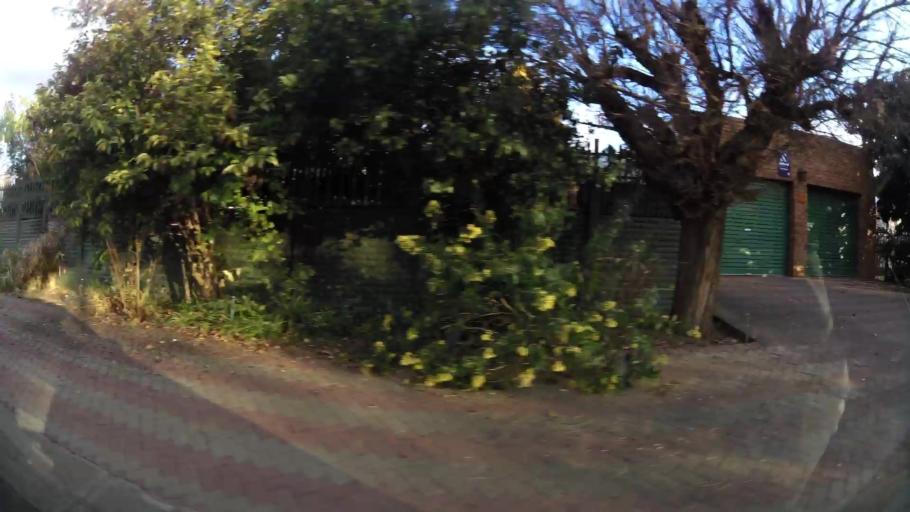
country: ZA
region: Orange Free State
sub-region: Mangaung Metropolitan Municipality
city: Bloemfontein
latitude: -29.1394
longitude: 26.1769
